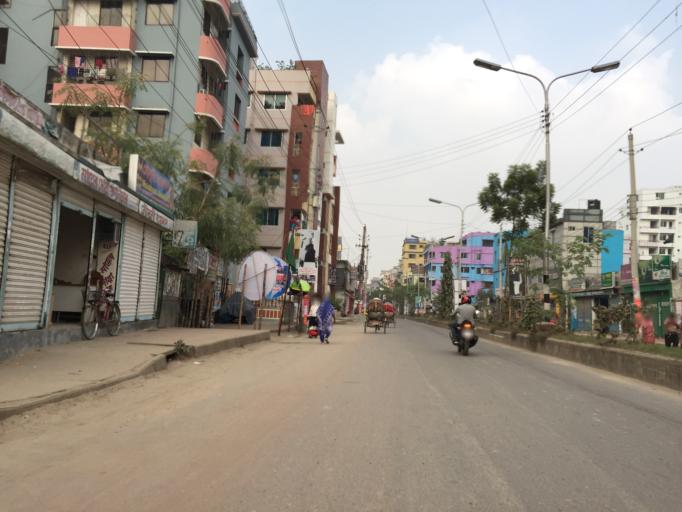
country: BD
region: Dhaka
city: Azimpur
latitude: 23.7809
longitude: 90.3685
